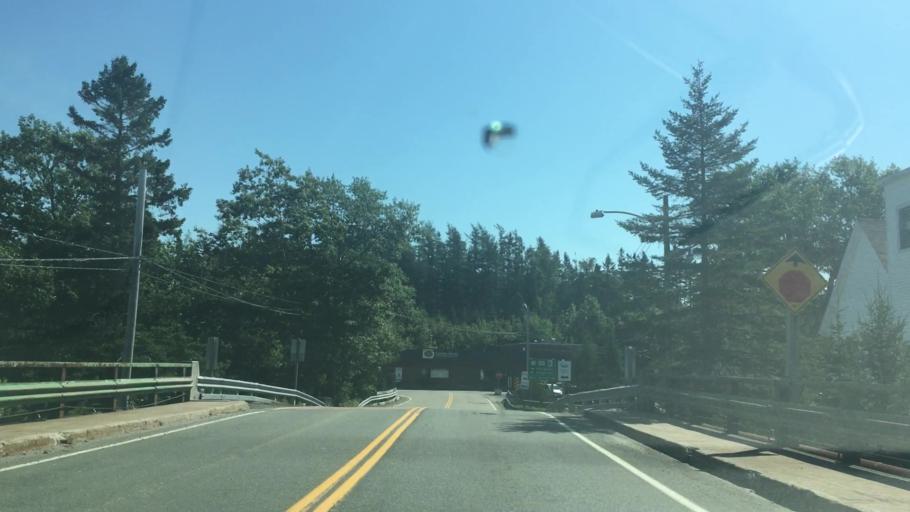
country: CA
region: Nova Scotia
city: Antigonish
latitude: 45.1431
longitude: -61.9838
